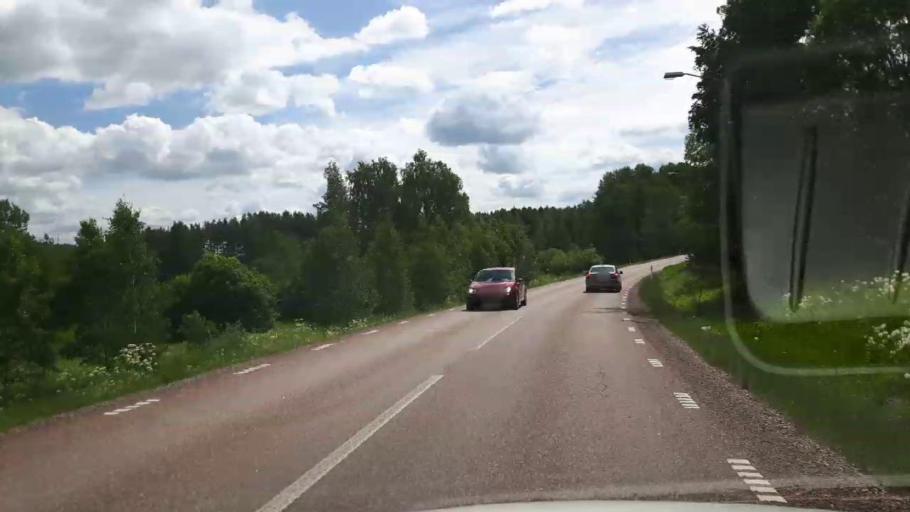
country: SE
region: Dalarna
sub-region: Saters Kommun
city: Saeter
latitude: 60.4209
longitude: 15.8461
